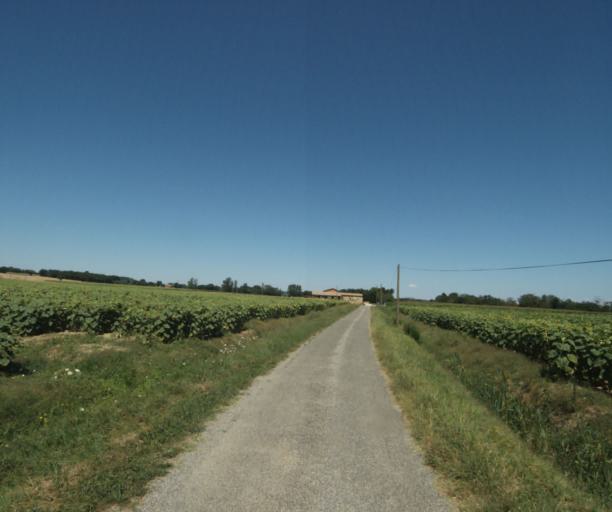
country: FR
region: Midi-Pyrenees
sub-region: Departement de la Haute-Garonne
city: Revel
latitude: 43.4858
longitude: 1.9479
